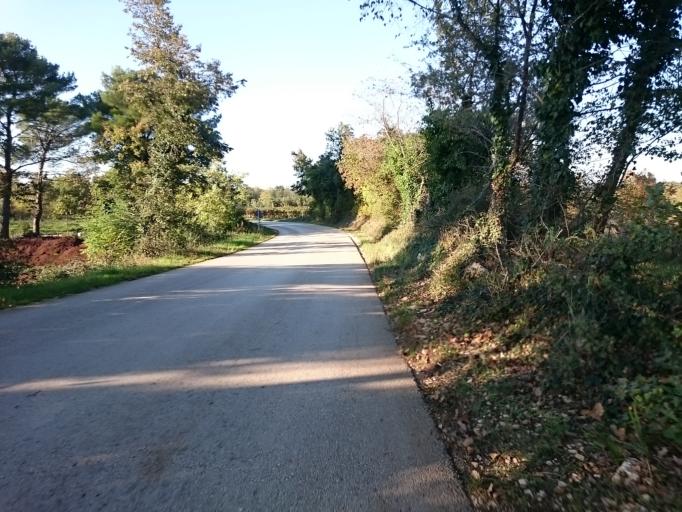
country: HR
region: Istarska
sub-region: Grad Porec
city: Porec
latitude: 45.2901
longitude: 13.6408
